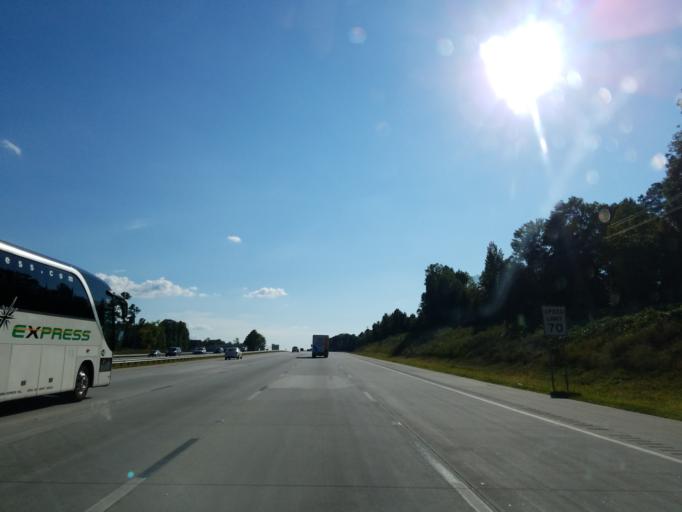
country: US
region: North Carolina
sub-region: Davidson County
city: Tyro
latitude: 35.7666
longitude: -80.3337
